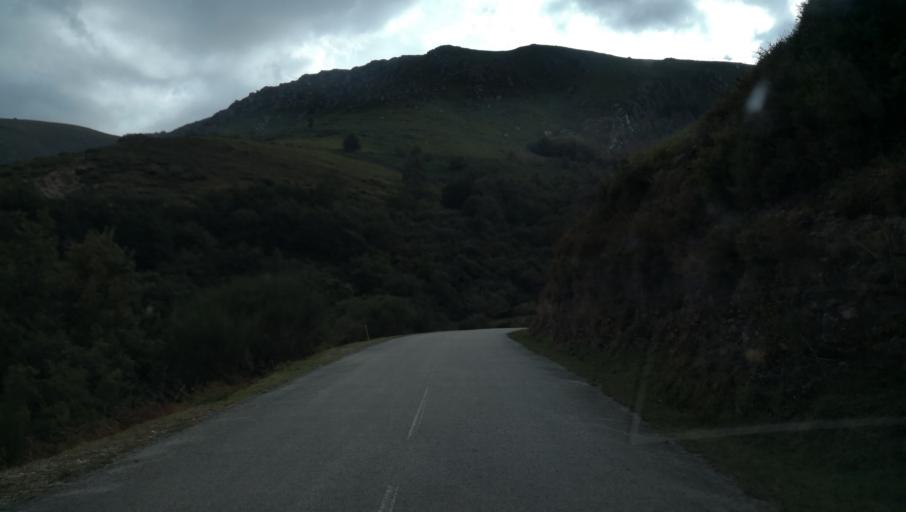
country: PT
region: Vila Real
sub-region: Mondim de Basto
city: Mondim de Basto
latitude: 41.3595
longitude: -7.8504
